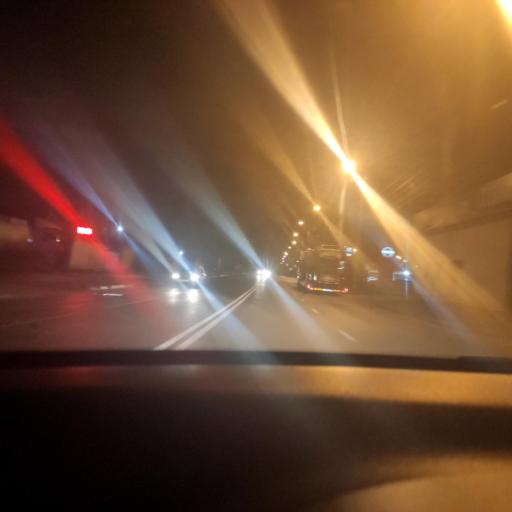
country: RU
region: Samara
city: Samara
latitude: 53.1832
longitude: 50.1522
